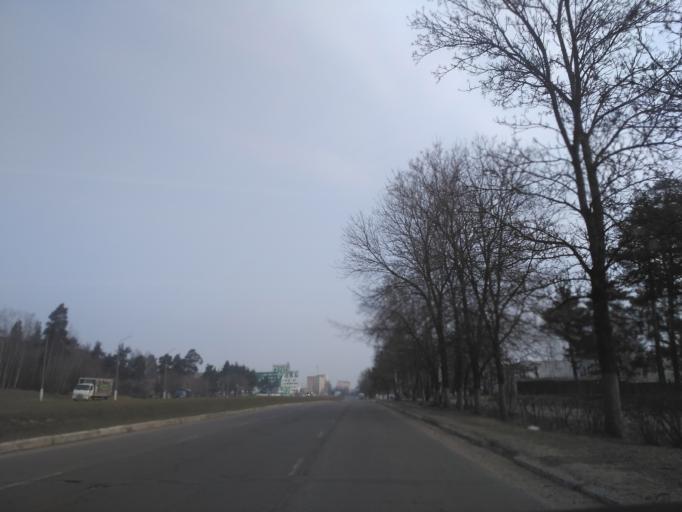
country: BY
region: Minsk
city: Horad Barysaw
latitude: 54.2006
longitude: 28.4974
